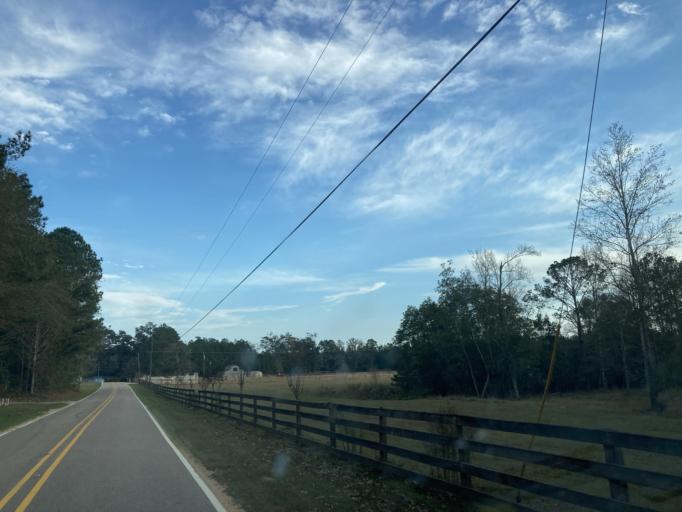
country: US
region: Mississippi
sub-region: Lamar County
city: Purvis
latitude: 31.1858
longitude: -89.3630
